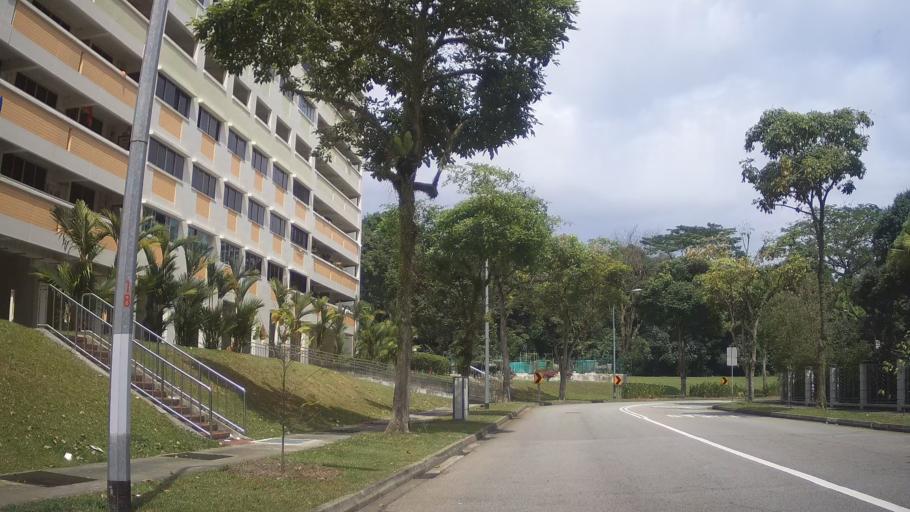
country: MY
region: Johor
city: Johor Bahru
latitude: 1.3793
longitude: 103.7743
